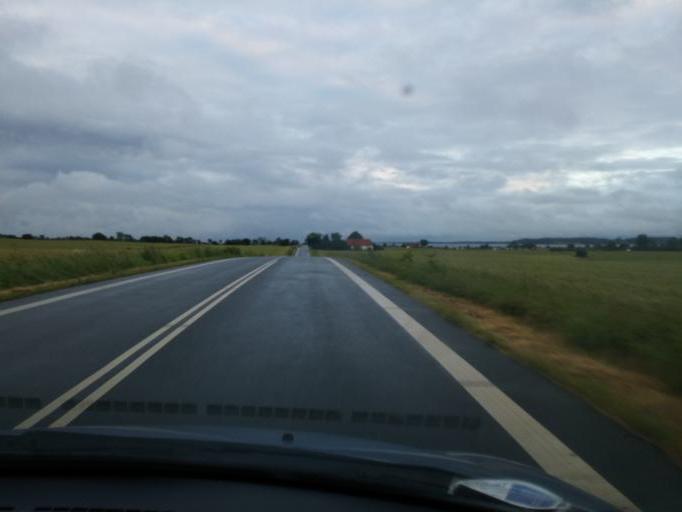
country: DK
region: South Denmark
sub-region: Kerteminde Kommune
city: Kerteminde
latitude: 55.4731
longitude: 10.6693
